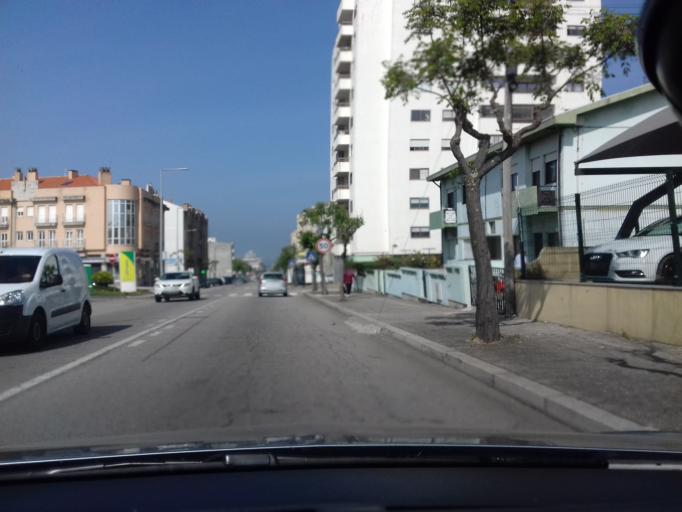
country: PT
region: Aveiro
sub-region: Espinho
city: Espinho
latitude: 41.0085
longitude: -8.6279
